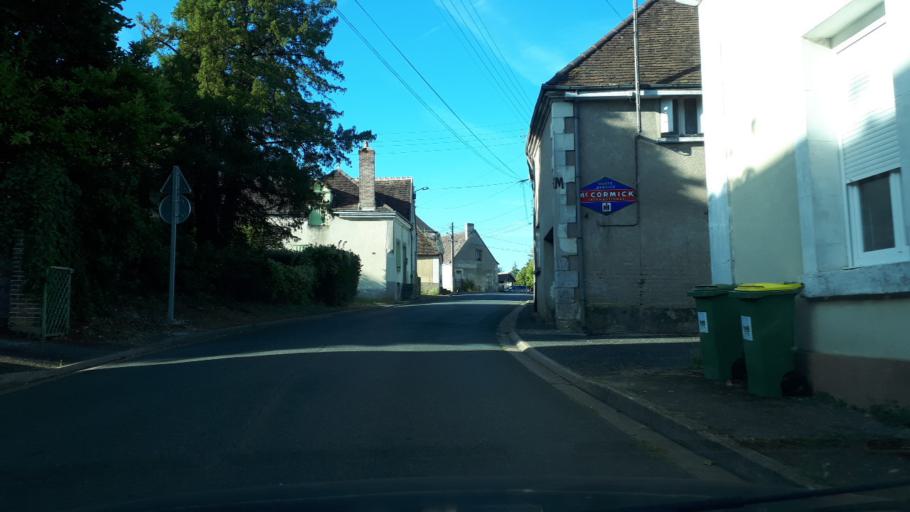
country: FR
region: Centre
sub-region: Departement d'Indre-et-Loire
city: Chateau-Renault
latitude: 47.6498
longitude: 0.9419
